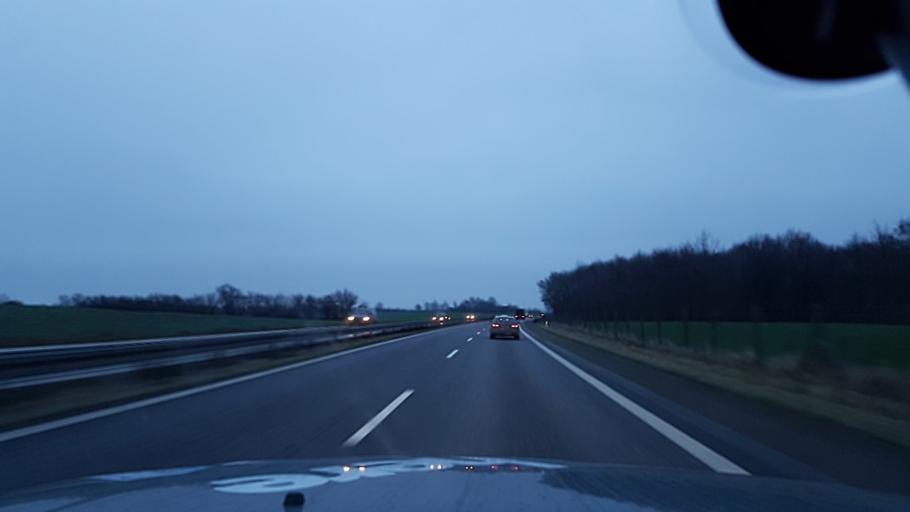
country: DK
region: Zealand
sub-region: Faxe Kommune
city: Ronnede
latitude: 55.2024
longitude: 11.9768
